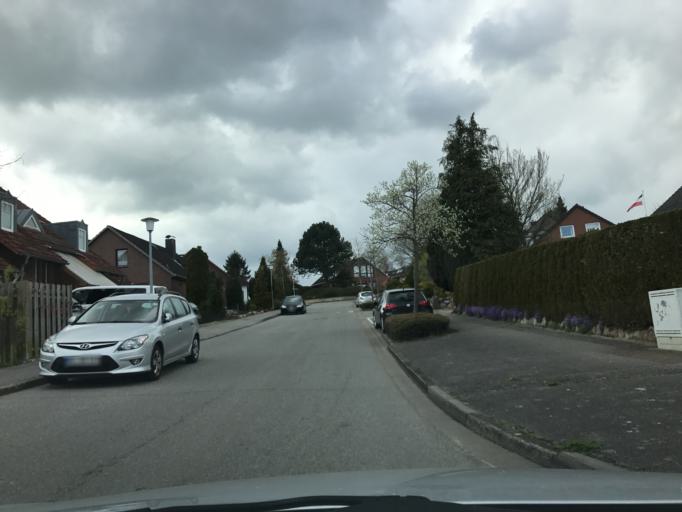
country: DE
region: Schleswig-Holstein
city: Neustadt in Holstein
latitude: 54.0940
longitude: 10.8295
